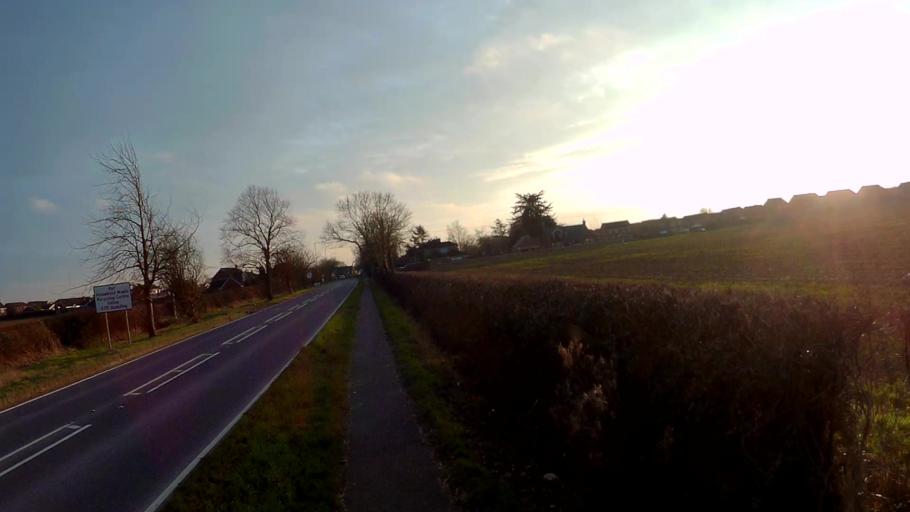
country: GB
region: England
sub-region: Lincolnshire
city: Bourne
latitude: 52.7804
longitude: -0.3769
